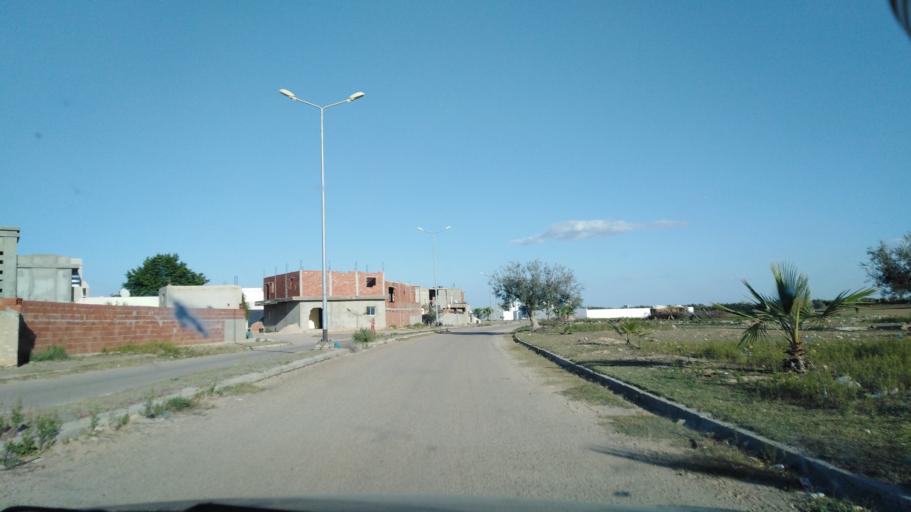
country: TN
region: Al Mahdiyah
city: Shurban
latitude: 34.9616
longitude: 10.3665
